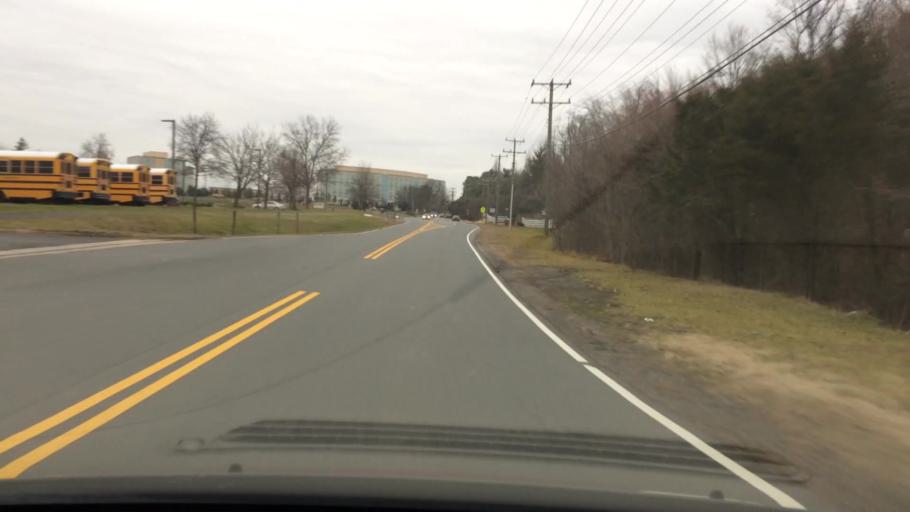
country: US
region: Virginia
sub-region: Fairfax County
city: Chantilly
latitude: 38.9066
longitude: -77.4186
